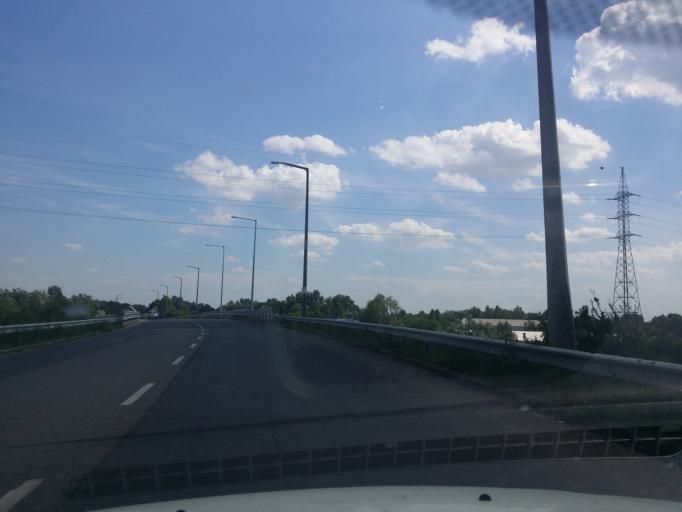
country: HU
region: Bacs-Kiskun
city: Kecskemet
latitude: 46.8984
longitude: 19.7039
